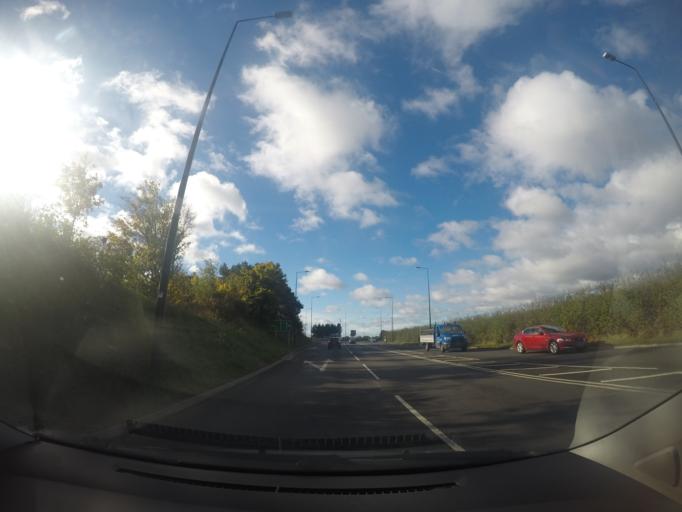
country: GB
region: England
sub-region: City of York
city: Skelton
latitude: 53.9877
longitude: -1.1215
